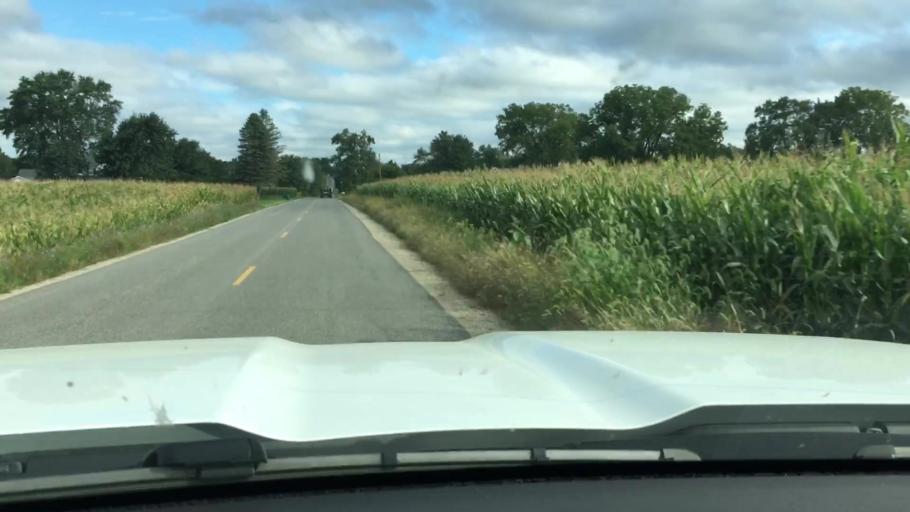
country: US
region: Michigan
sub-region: Kent County
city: Byron Center
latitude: 42.7866
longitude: -85.8026
